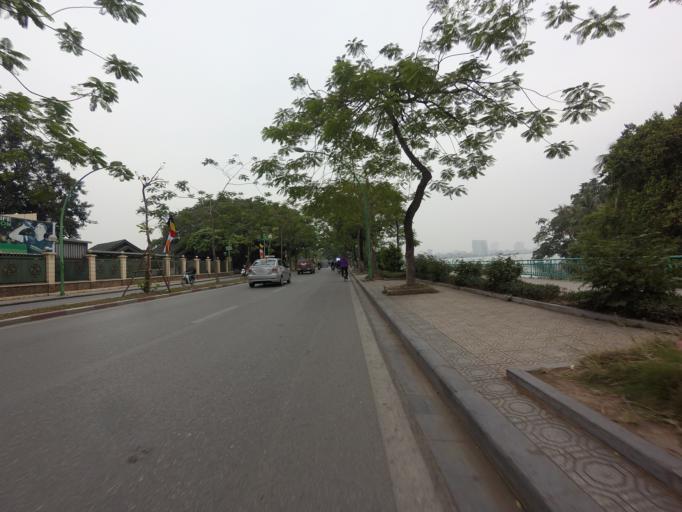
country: VN
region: Ha Noi
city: Hoan Kiem
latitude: 21.0477
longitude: 105.8373
